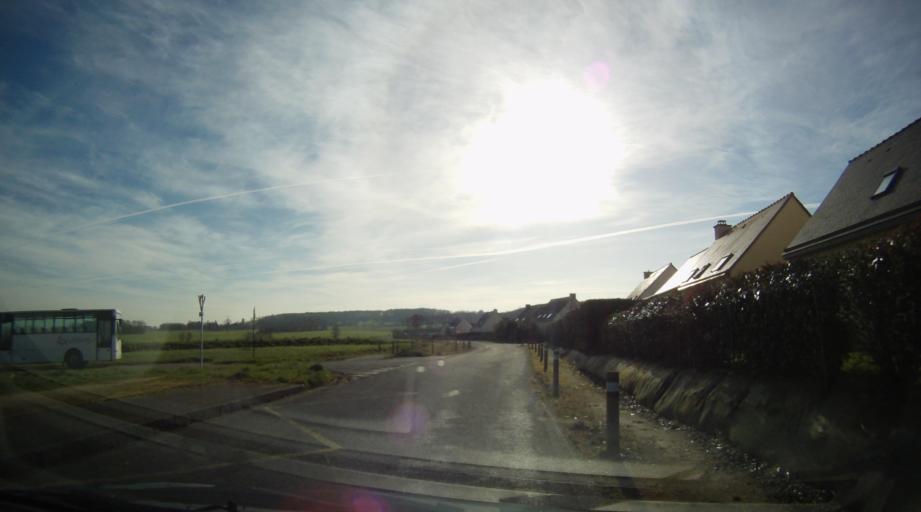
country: FR
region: Brittany
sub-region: Departement d'Ille-et-Vilaine
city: Orgeres
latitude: 47.9938
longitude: -1.6654
